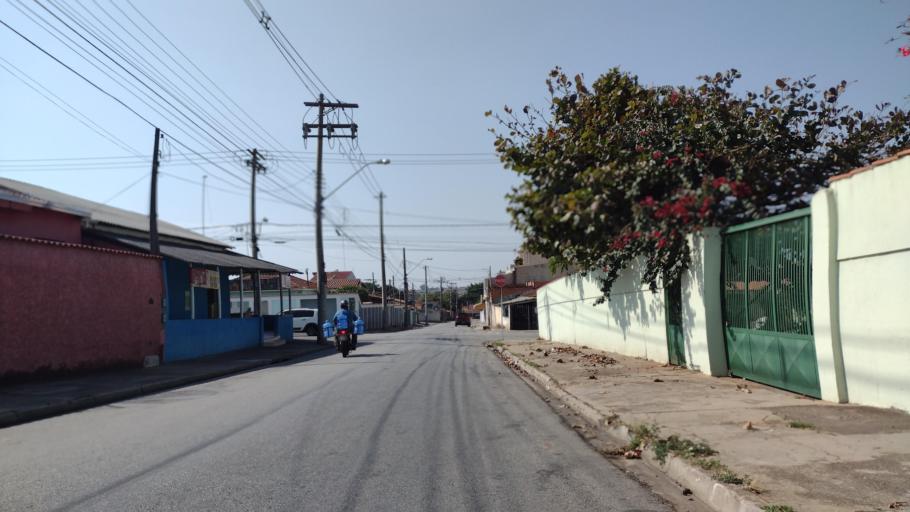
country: BR
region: Sao Paulo
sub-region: Sorocaba
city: Sorocaba
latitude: -23.4182
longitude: -47.4120
